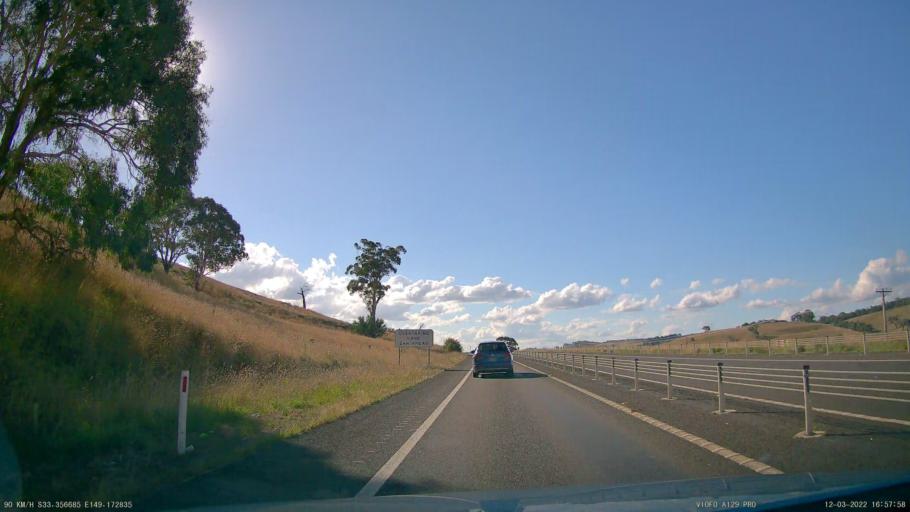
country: AU
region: New South Wales
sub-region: Blayney
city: Millthorpe
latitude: -33.3567
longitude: 149.1725
